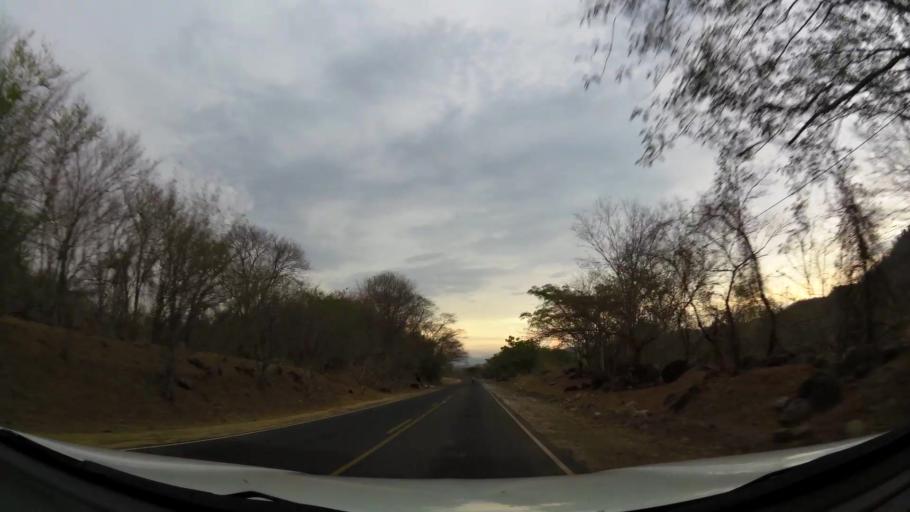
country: NI
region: Leon
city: La Jicaral
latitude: 12.7065
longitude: -86.3965
